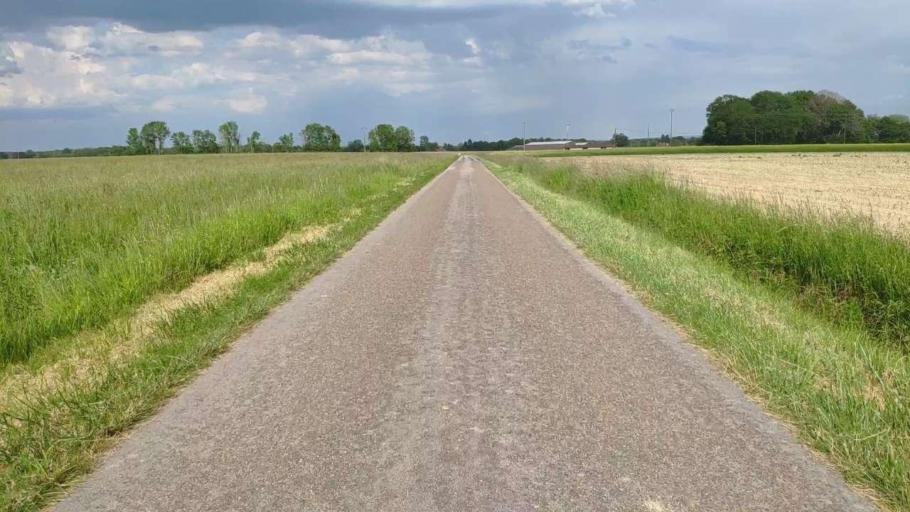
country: FR
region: Franche-Comte
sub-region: Departement du Jura
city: Bletterans
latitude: 46.8144
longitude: 5.3829
